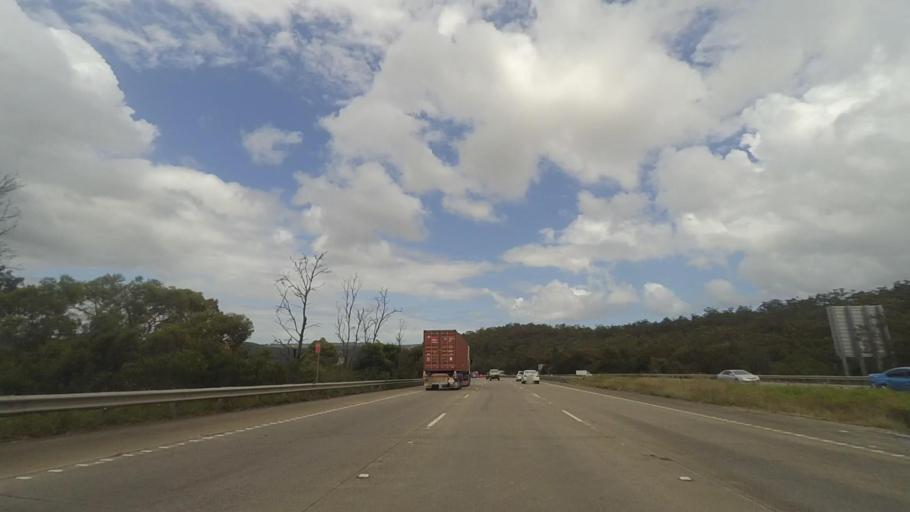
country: AU
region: New South Wales
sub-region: Gosford Shire
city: Point Clare
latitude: -33.4278
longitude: 151.2393
